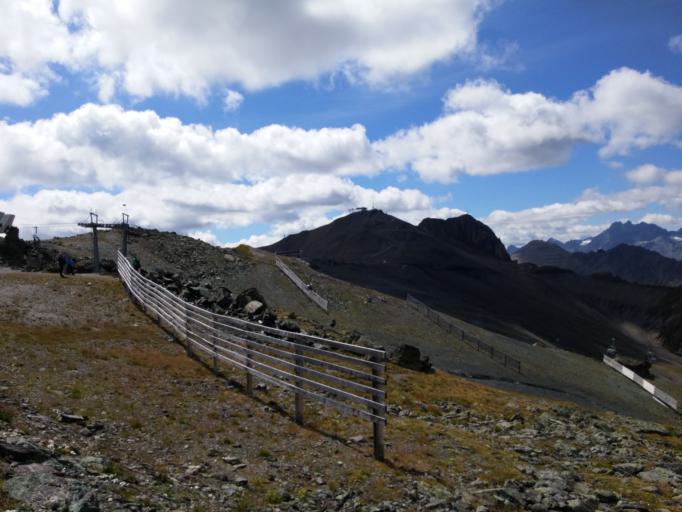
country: AT
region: Tyrol
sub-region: Politischer Bezirk Landeck
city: Ischgl
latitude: 46.9809
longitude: 10.3392
